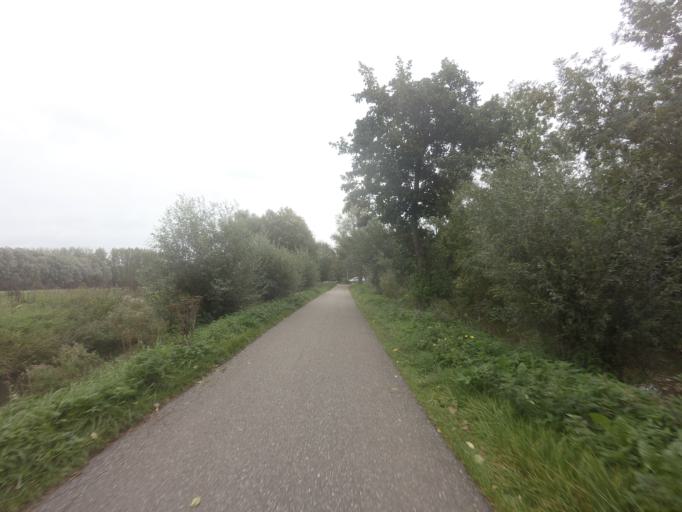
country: NL
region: Friesland
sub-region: Gemeente Leeuwarden
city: Bilgaard
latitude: 53.2201
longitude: 5.7914
